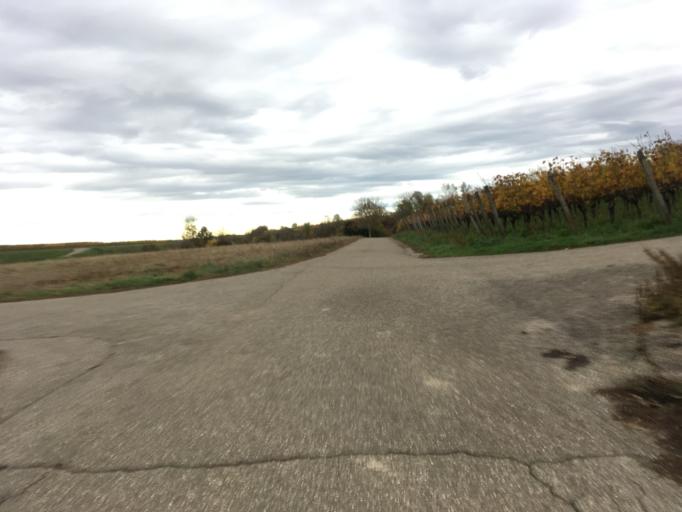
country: DE
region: Baden-Wuerttemberg
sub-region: Freiburg Region
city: Gottenheim
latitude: 48.0360
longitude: 7.7191
